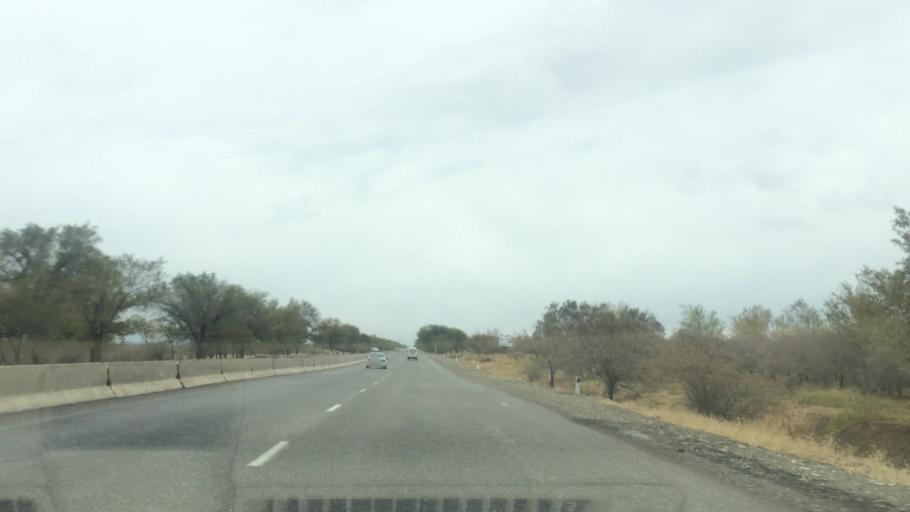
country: UZ
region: Samarqand
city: Bulung'ur
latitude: 39.8157
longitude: 67.3780
